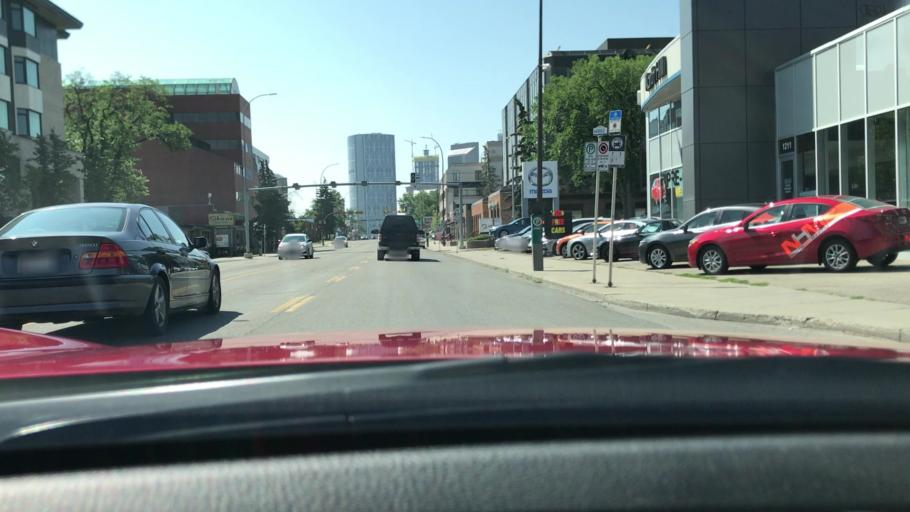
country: CA
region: Alberta
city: Calgary
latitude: 51.0631
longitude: -114.0626
